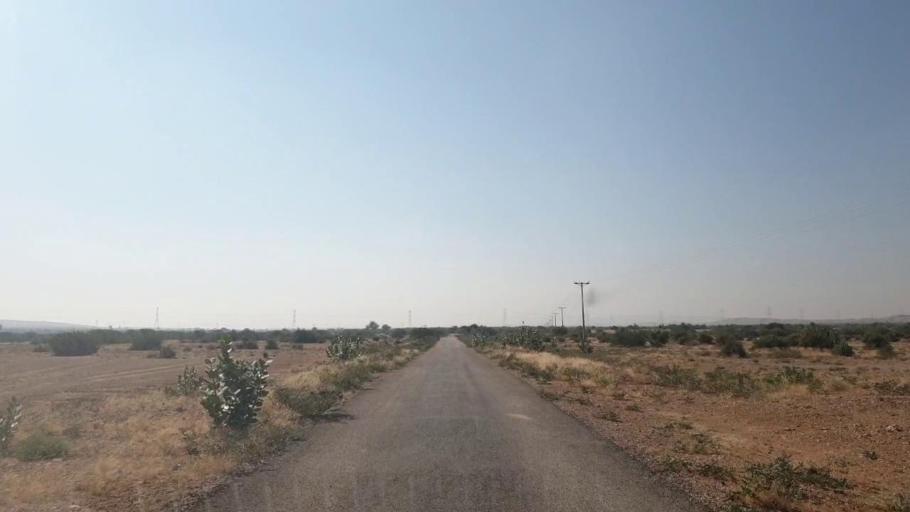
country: PK
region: Sindh
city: Thatta
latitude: 25.2164
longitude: 67.7494
